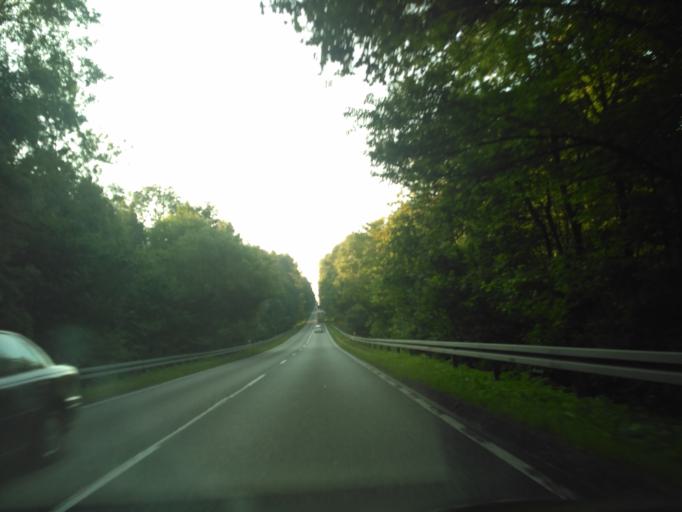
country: PL
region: Lublin Voivodeship
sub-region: Powiat krasnicki
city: Szastarka
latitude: 50.8554
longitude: 22.2847
